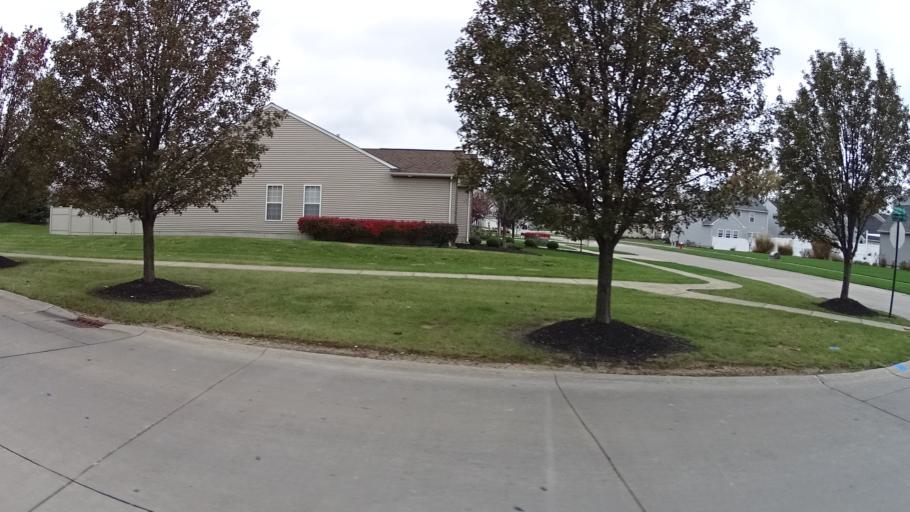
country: US
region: Ohio
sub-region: Lorain County
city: Amherst
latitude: 41.4279
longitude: -82.2220
